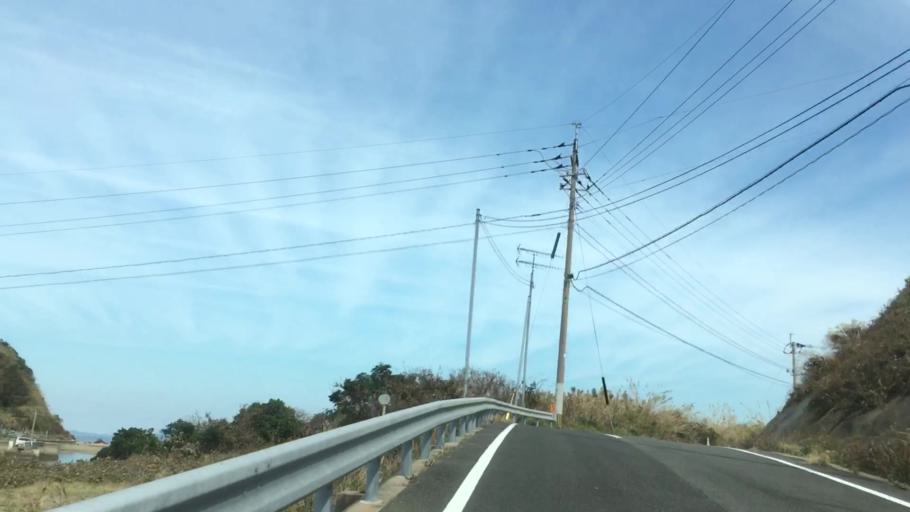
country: JP
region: Nagasaki
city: Sasebo
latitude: 33.0048
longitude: 129.5557
